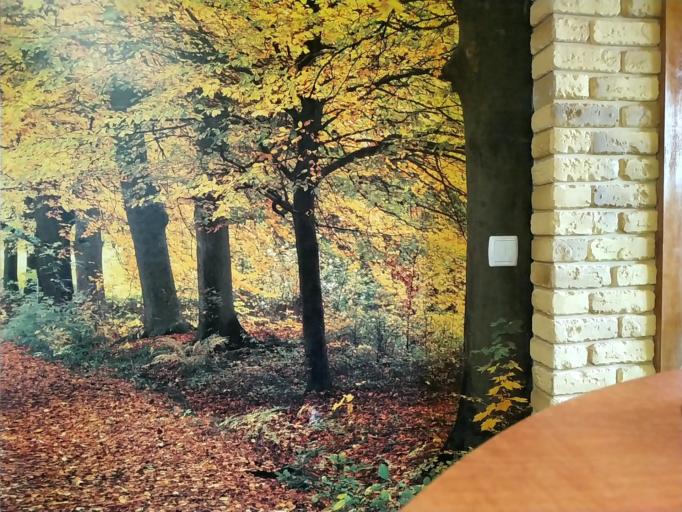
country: RU
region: Novgorod
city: Opechenskiy Posad
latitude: 58.2703
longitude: 34.0102
